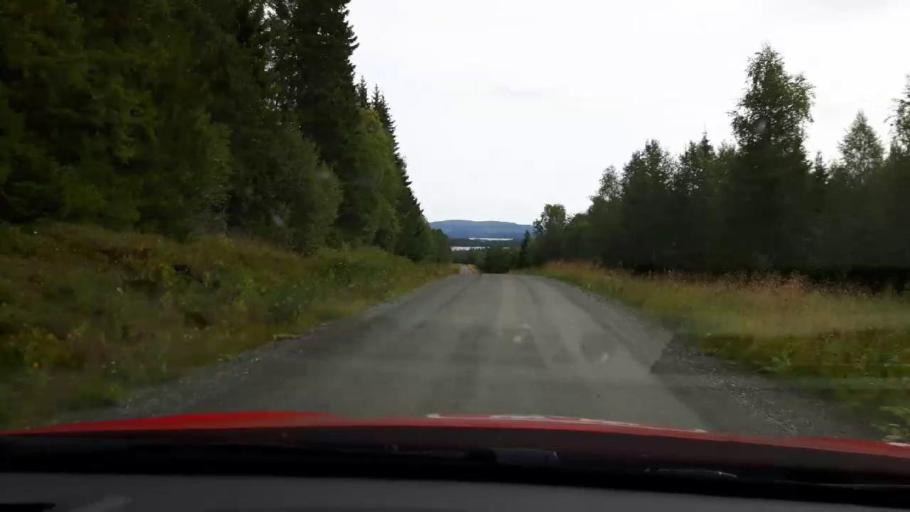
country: SE
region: Jaemtland
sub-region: Are Kommun
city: Are
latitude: 63.7474
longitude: 12.9681
